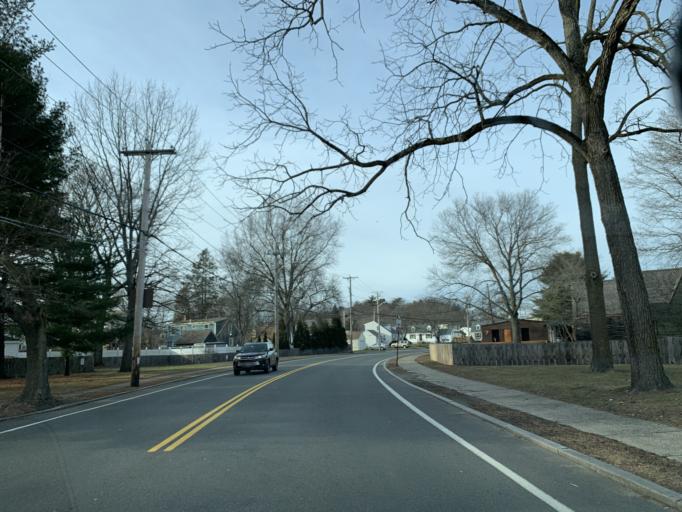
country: US
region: Massachusetts
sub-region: Essex County
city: Saugus
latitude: 42.4680
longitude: -71.0090
